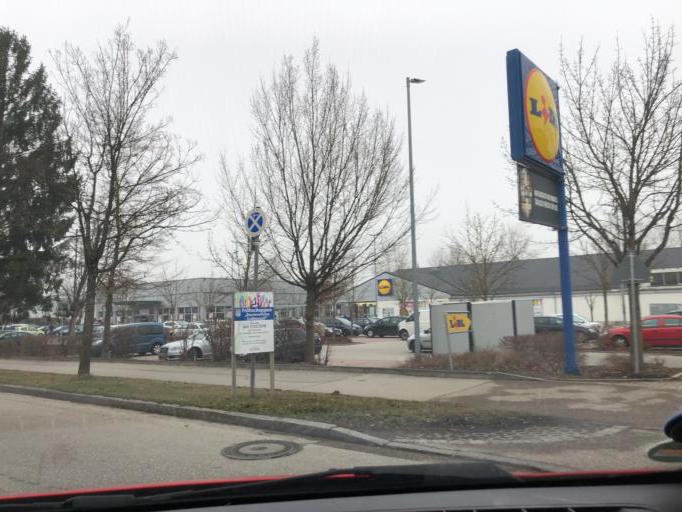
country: DE
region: Bavaria
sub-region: Upper Bavaria
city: Grobenzell
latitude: 48.1840
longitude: 11.3873
